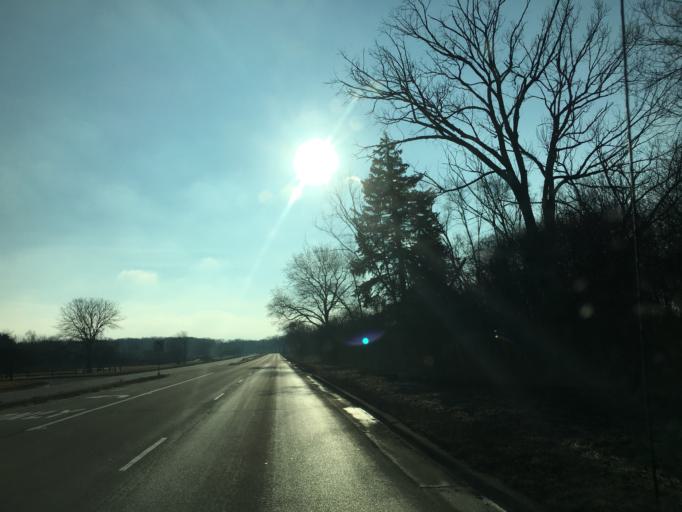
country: US
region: Illinois
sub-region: Cook County
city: Rolling Meadows
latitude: 42.0325
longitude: -88.0150
